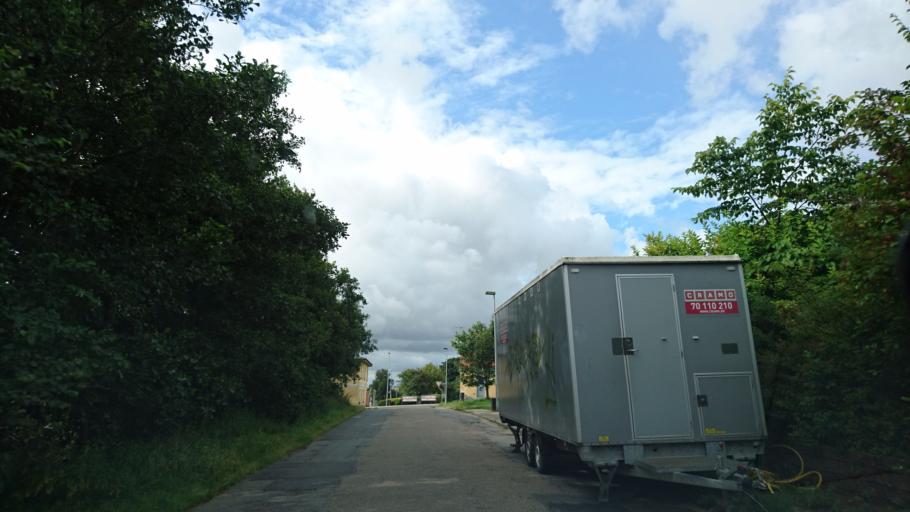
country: DK
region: North Denmark
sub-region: Hjorring Kommune
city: Tars
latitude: 57.3667
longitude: 10.1883
